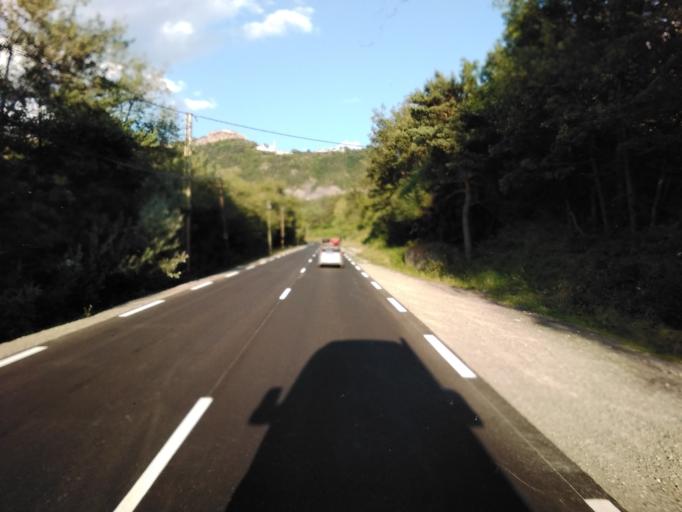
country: FR
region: Provence-Alpes-Cote d'Azur
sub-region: Departement des Alpes-de-Haute-Provence
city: Seyne-les-Alpes
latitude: 44.4472
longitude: 6.3595
